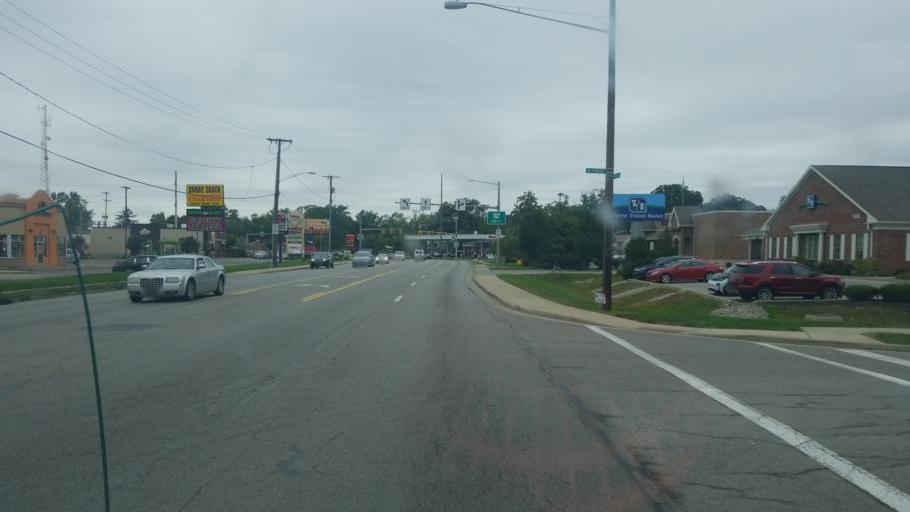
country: US
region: Ohio
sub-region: Lucas County
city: Ottawa Hills
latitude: 41.6518
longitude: -83.6646
